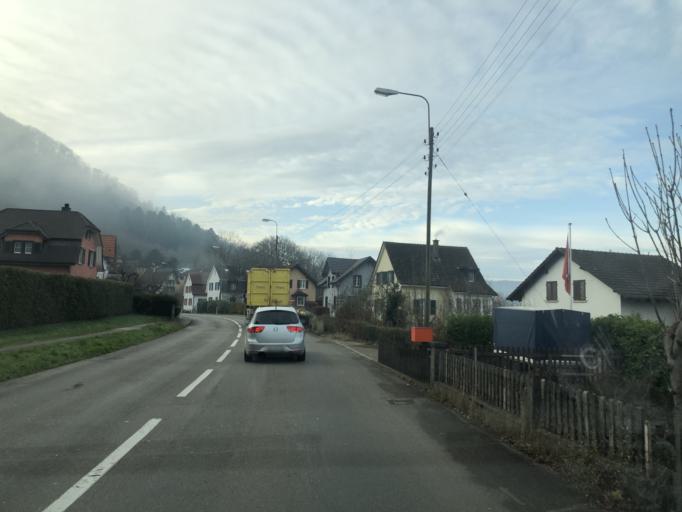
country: CH
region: Aargau
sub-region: Bezirk Baden
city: Turgi
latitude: 47.4891
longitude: 8.2568
